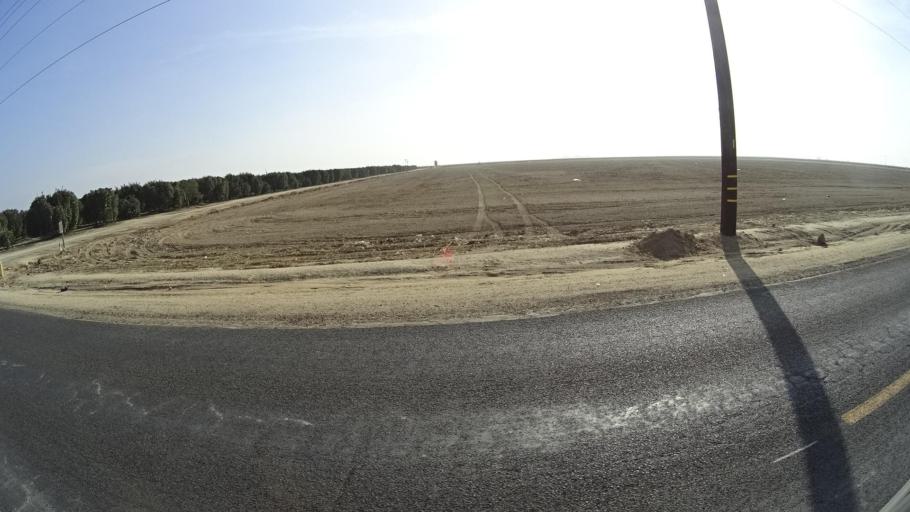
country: US
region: California
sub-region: Tulare County
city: Richgrove
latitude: 35.7760
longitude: -119.1654
